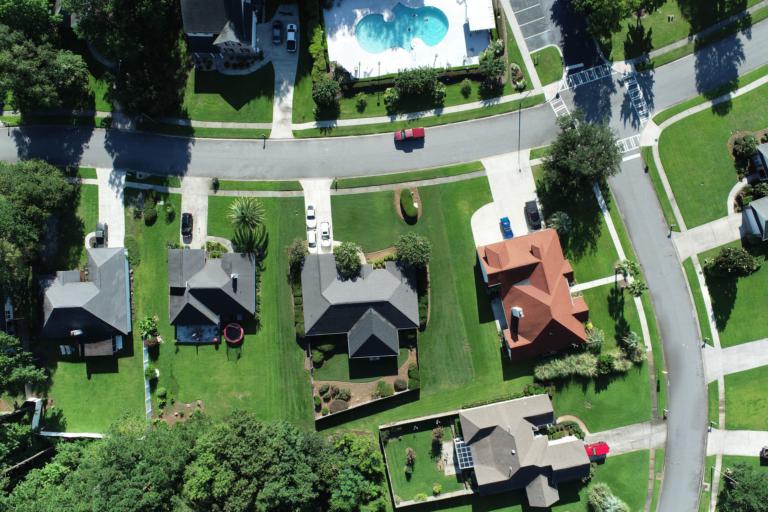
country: US
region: Georgia
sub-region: Chatham County
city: Georgetown
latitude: 32.0085
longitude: -81.2592
